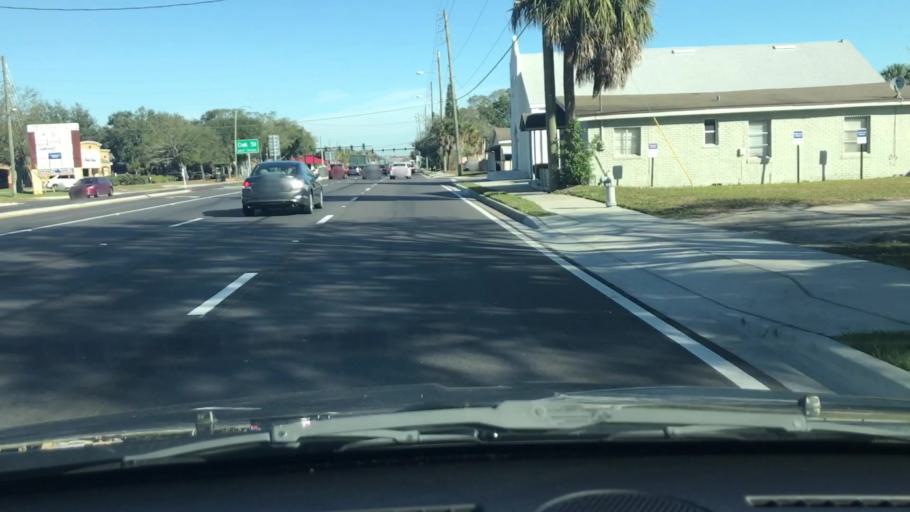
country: US
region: Florida
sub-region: Osceola County
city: Kissimmee
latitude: 28.2985
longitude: -81.4159
